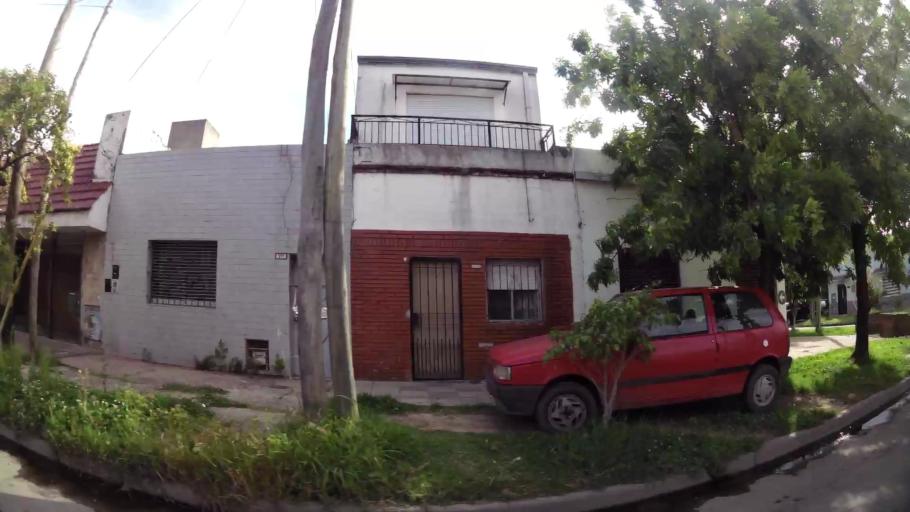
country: AR
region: Buenos Aires
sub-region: Partido de Lanus
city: Lanus
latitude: -34.6944
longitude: -58.3781
